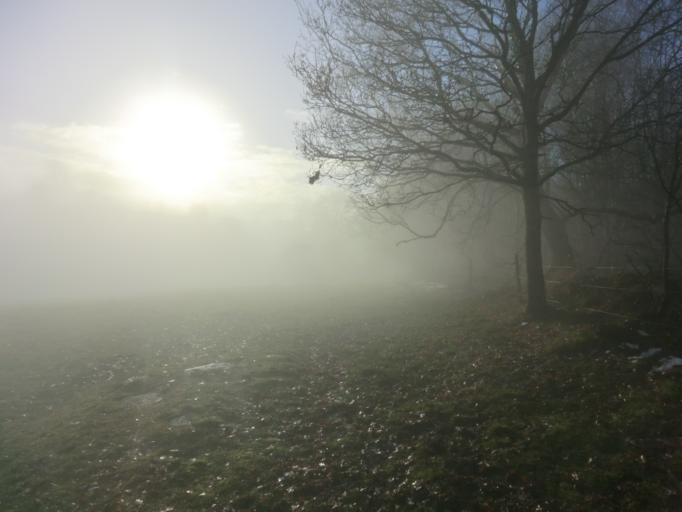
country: SE
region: Skane
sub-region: Lunds Kommun
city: Genarp
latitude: 55.7003
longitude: 13.3692
